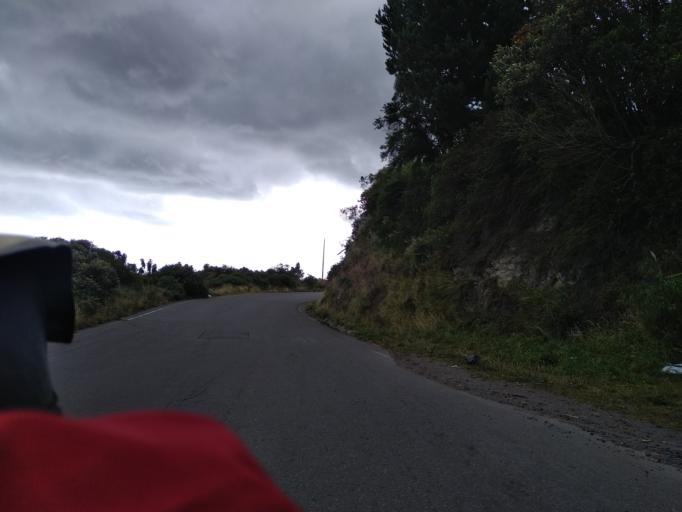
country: EC
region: Cotopaxi
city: Saquisili
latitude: -0.7236
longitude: -78.7611
